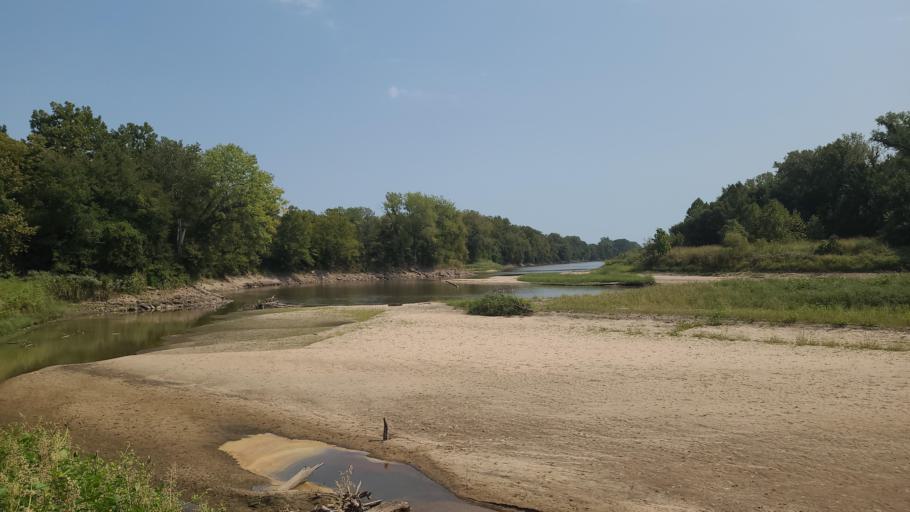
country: US
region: Kansas
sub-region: Douglas County
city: Lawrence
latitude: 38.9813
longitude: -95.1631
